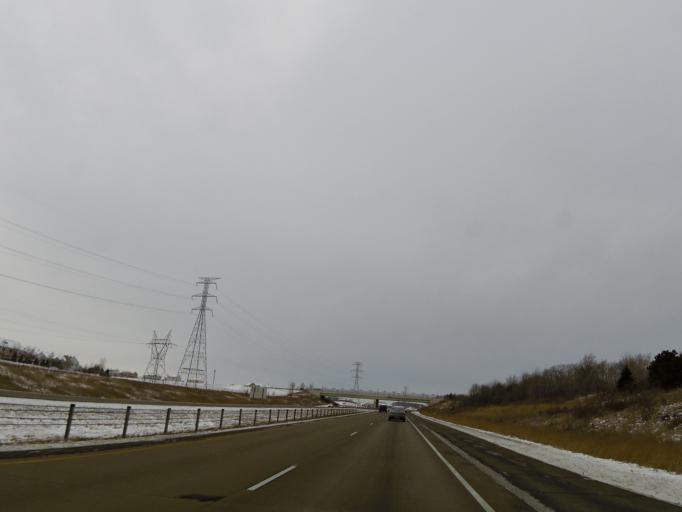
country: US
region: Minnesota
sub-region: Scott County
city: Shakopee
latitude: 44.7769
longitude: -93.5165
